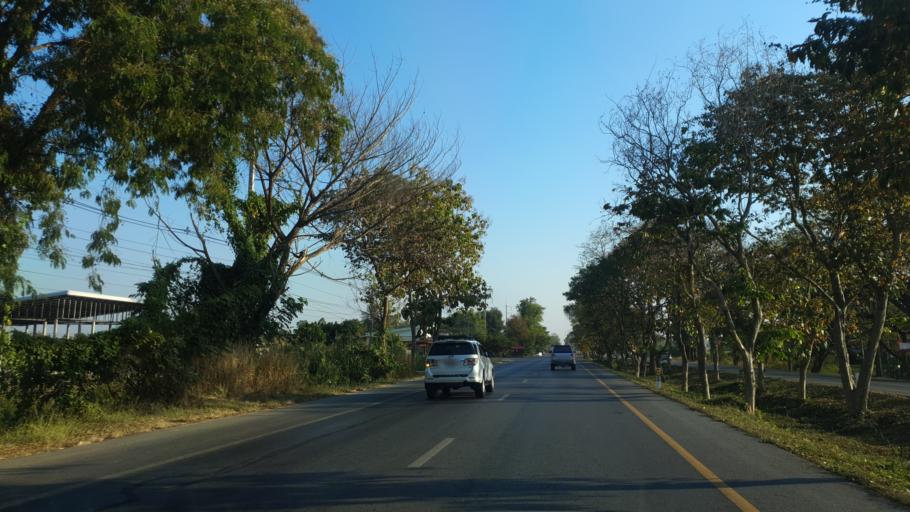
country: TH
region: Kamphaeng Phet
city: Khlong Khlung
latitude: 16.2398
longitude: 99.6939
